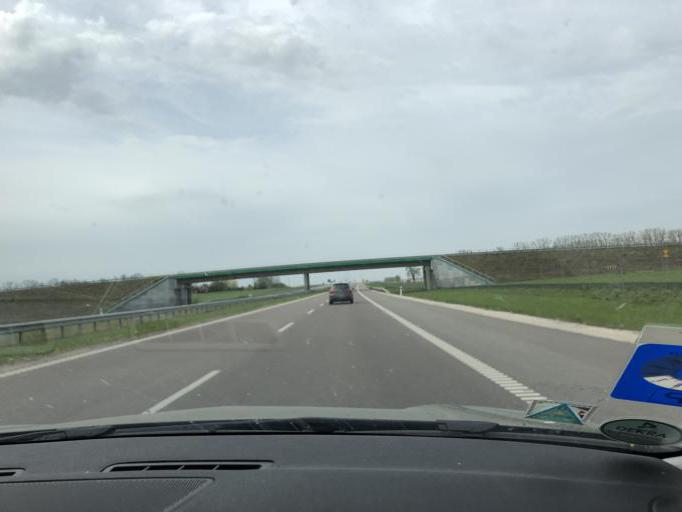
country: PL
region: Subcarpathian Voivodeship
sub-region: Powiat przemyski
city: Stubno
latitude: 49.9438
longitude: 22.9987
